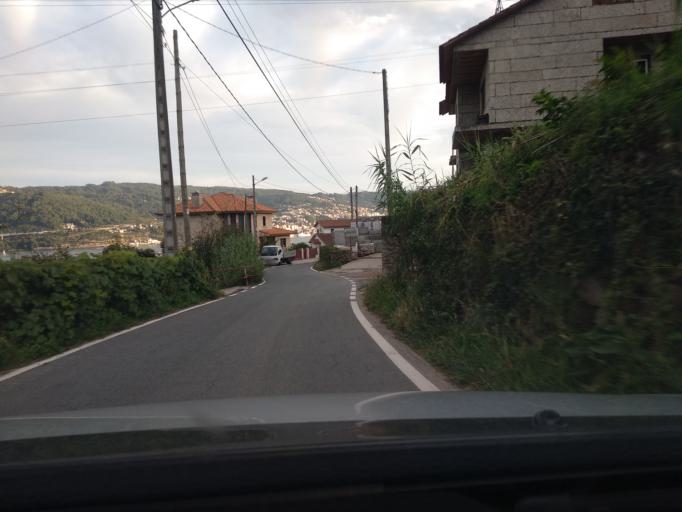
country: ES
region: Galicia
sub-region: Provincia de Pontevedra
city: Moana
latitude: 42.2933
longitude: -8.6821
